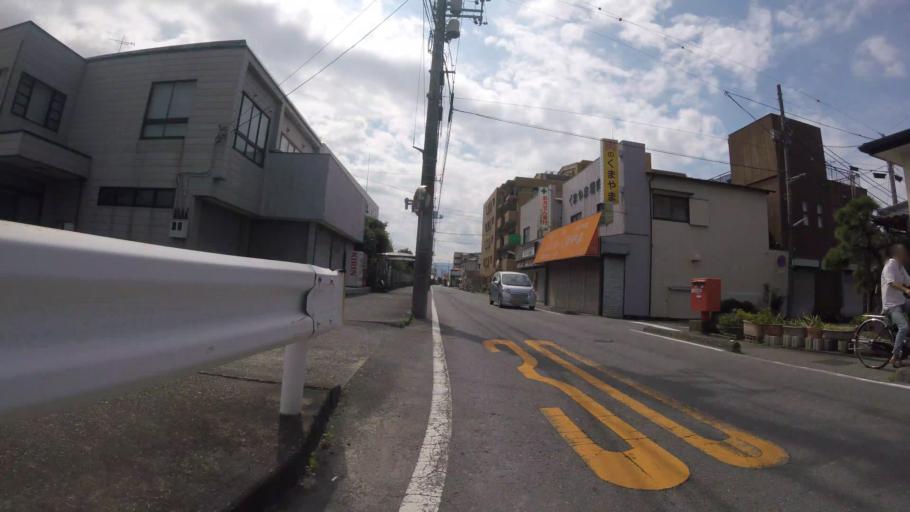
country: JP
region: Shizuoka
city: Numazu
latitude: 35.1161
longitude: 138.8713
